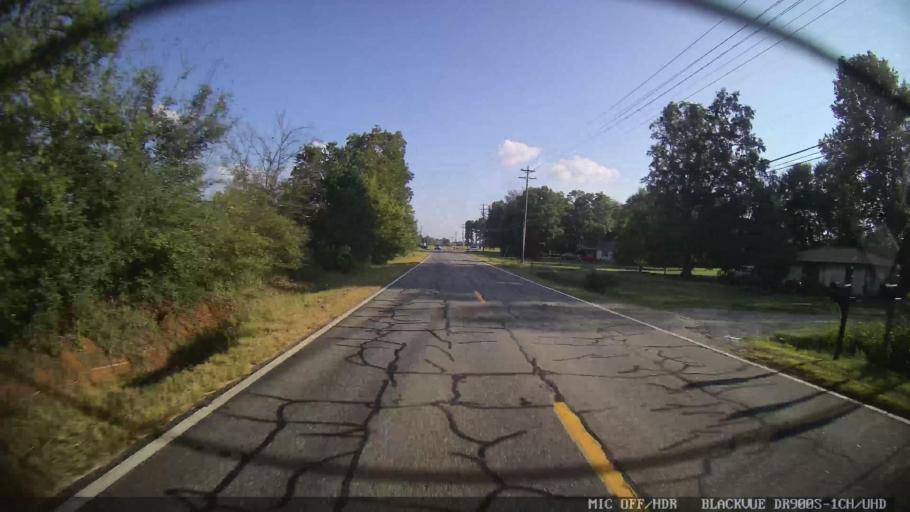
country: US
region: Georgia
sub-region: Murray County
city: Chatsworth
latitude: 34.7704
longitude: -84.8236
